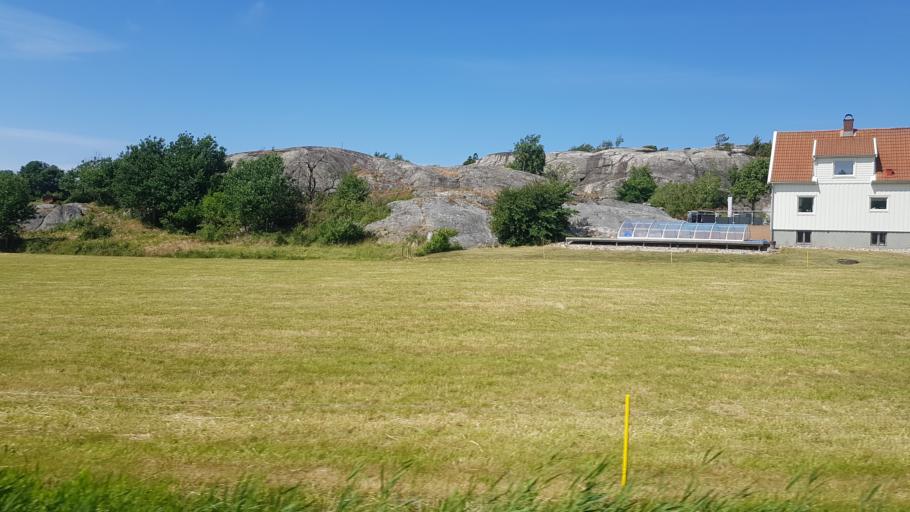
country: SE
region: Vaestra Goetaland
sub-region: Tjorns Kommun
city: Skaerhamn
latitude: 57.9835
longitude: 11.5687
